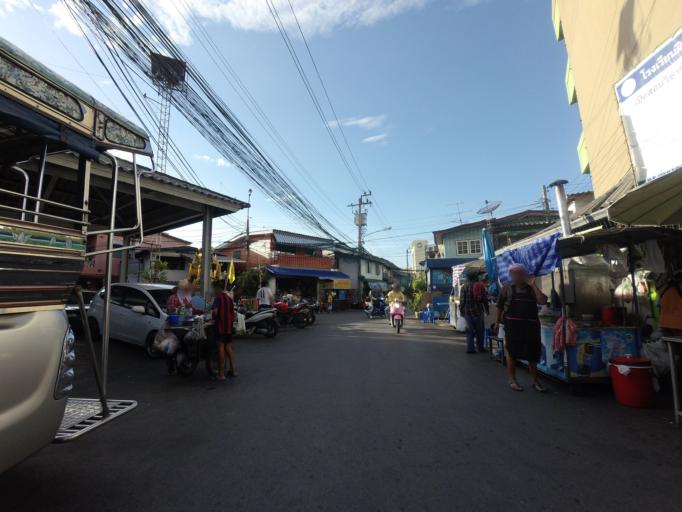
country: TH
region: Bangkok
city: Khlong Toei
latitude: 13.7107
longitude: 100.5763
